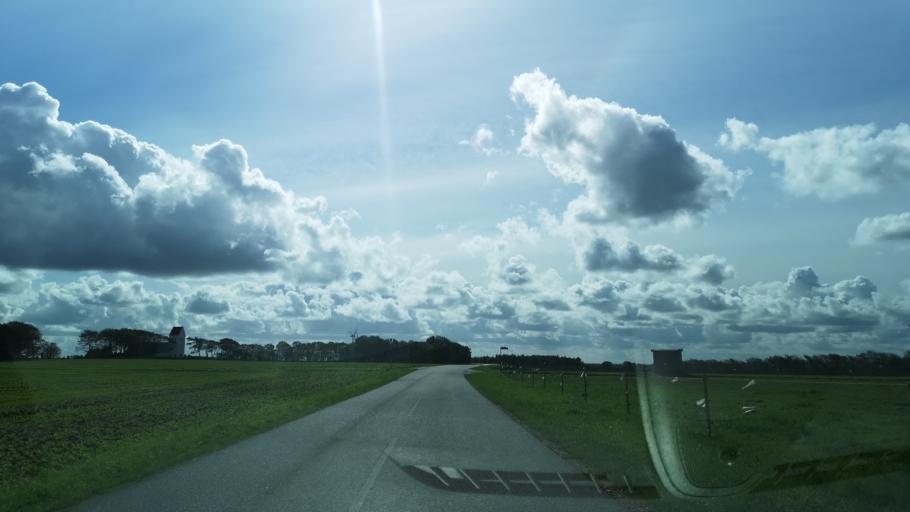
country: DK
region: Central Jutland
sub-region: Ringkobing-Skjern Kommune
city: Skjern
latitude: 55.9801
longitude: 8.5510
